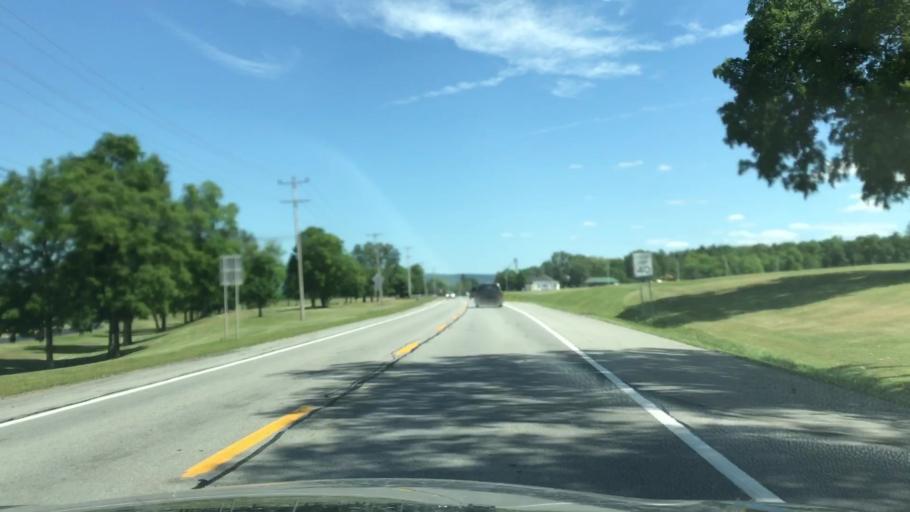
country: US
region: New York
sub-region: Livingston County
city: Mount Morris
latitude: 42.6821
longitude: -77.8263
